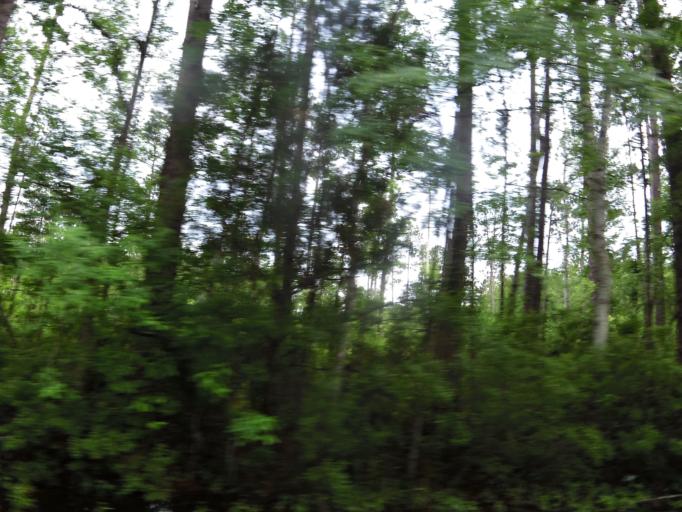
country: US
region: Florida
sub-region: Nassau County
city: Nassau Village-Ratliff
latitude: 30.5506
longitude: -81.7069
